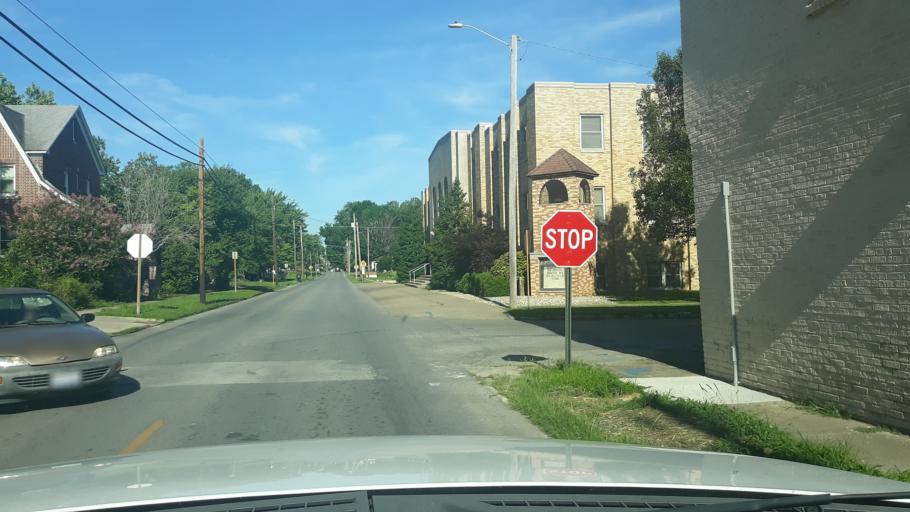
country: US
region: Illinois
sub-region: Saline County
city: Harrisburg
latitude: 37.7317
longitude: -88.5467
